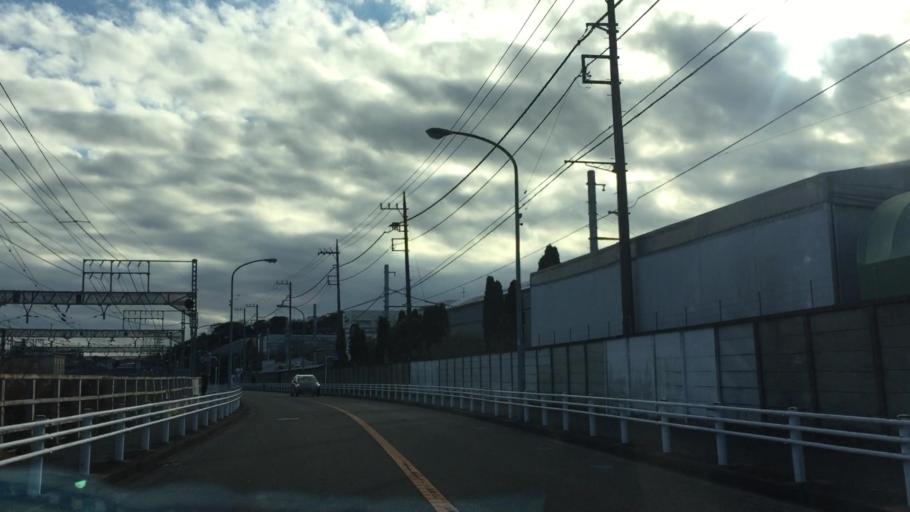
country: JP
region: Kanagawa
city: Zushi
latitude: 35.3372
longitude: 139.6199
